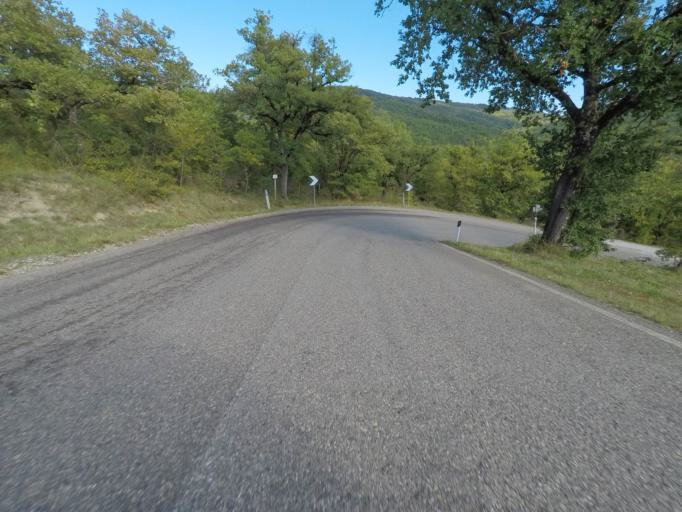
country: IT
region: Tuscany
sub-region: Provincia di Siena
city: Radda in Chianti
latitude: 43.5125
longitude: 11.4078
